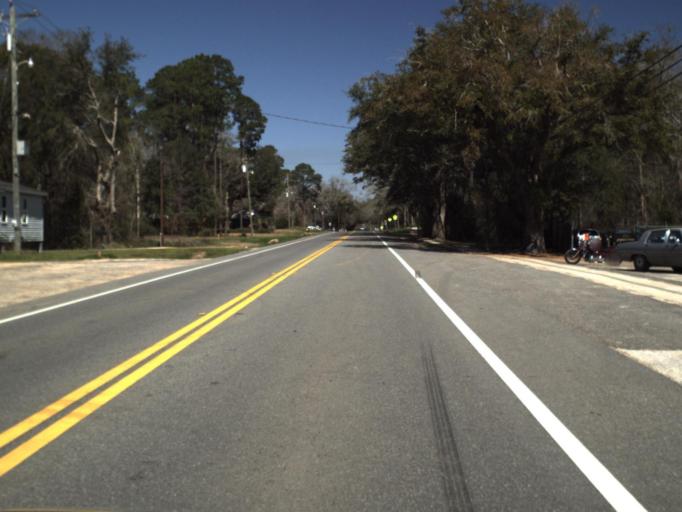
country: US
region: Florida
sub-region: Jackson County
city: Sneads
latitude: 30.7052
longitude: -85.0202
